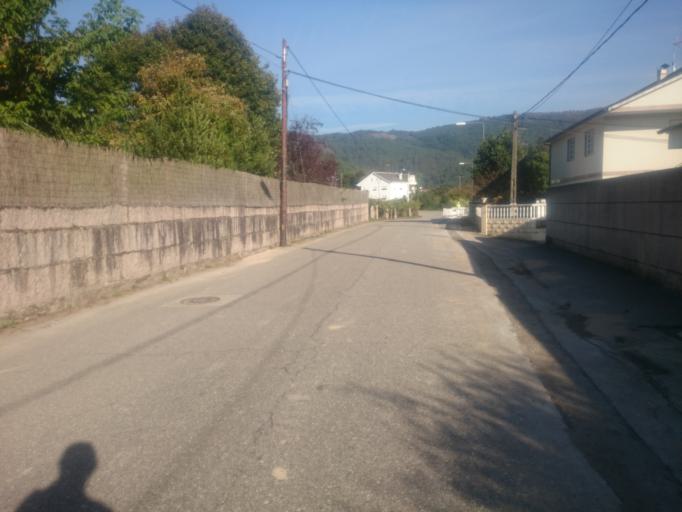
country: ES
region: Galicia
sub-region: Provincia de Pontevedra
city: Porrino
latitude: 42.1575
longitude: -8.6129
